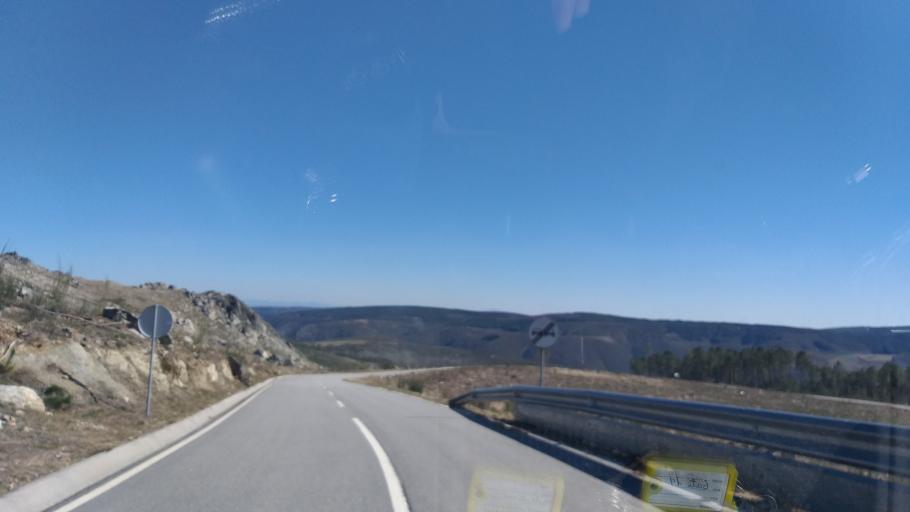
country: PT
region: Guarda
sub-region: Manteigas
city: Manteigas
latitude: 40.4784
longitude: -7.5101
